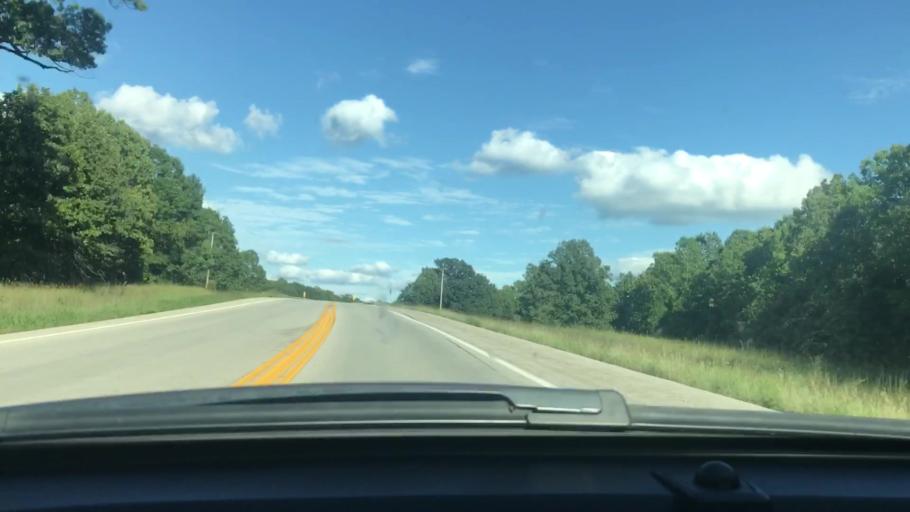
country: US
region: Missouri
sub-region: Howell County
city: West Plains
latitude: 36.6606
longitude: -91.7166
